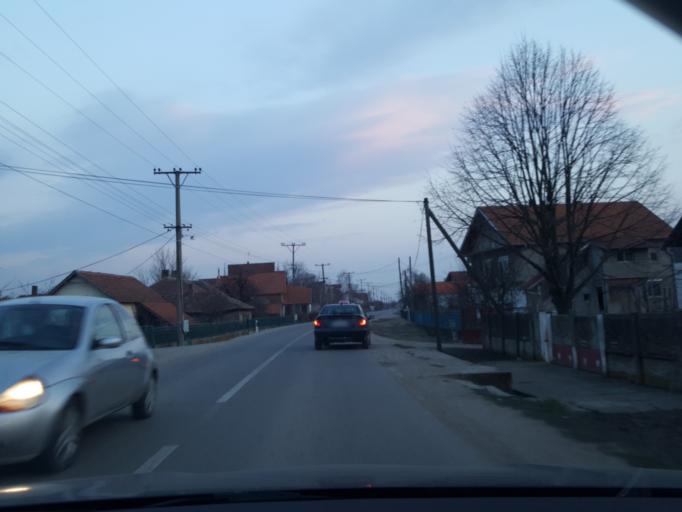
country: RS
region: Central Serbia
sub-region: Nisavski Okrug
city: Aleksinac
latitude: 43.4999
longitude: 21.7041
